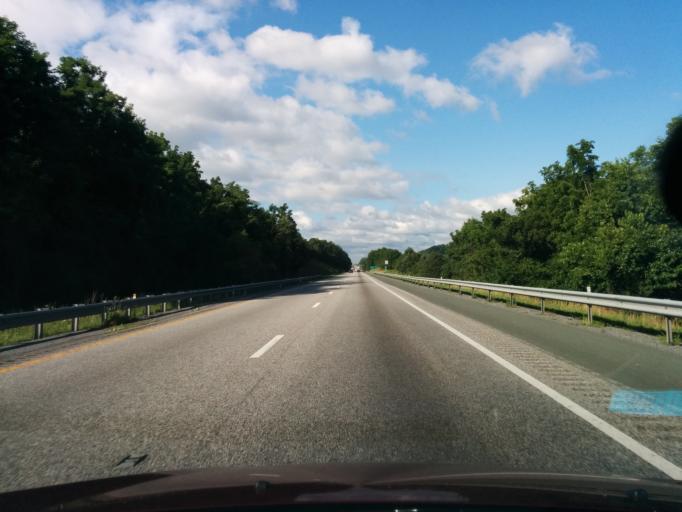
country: US
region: Virginia
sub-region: City of Lexington
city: Lexington
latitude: 37.7492
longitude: -79.4159
